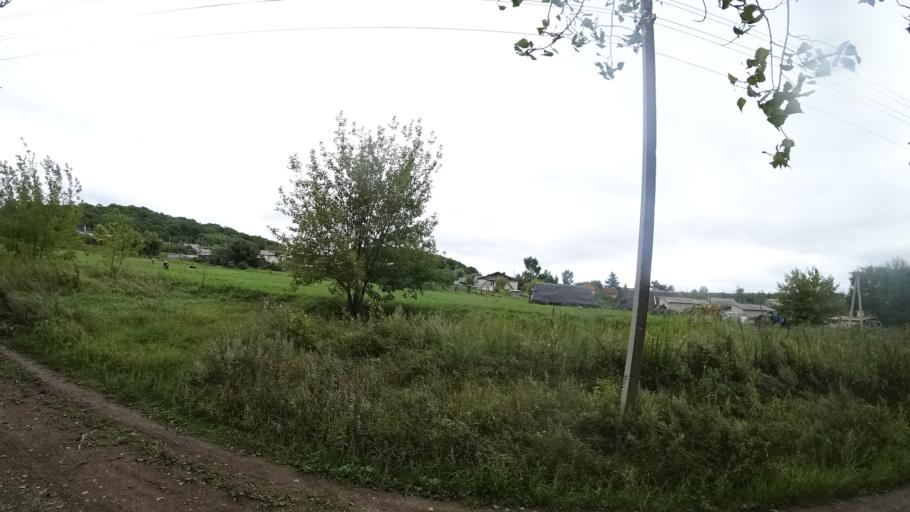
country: RU
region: Primorskiy
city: Chernigovka
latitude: 44.4587
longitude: 132.5944
